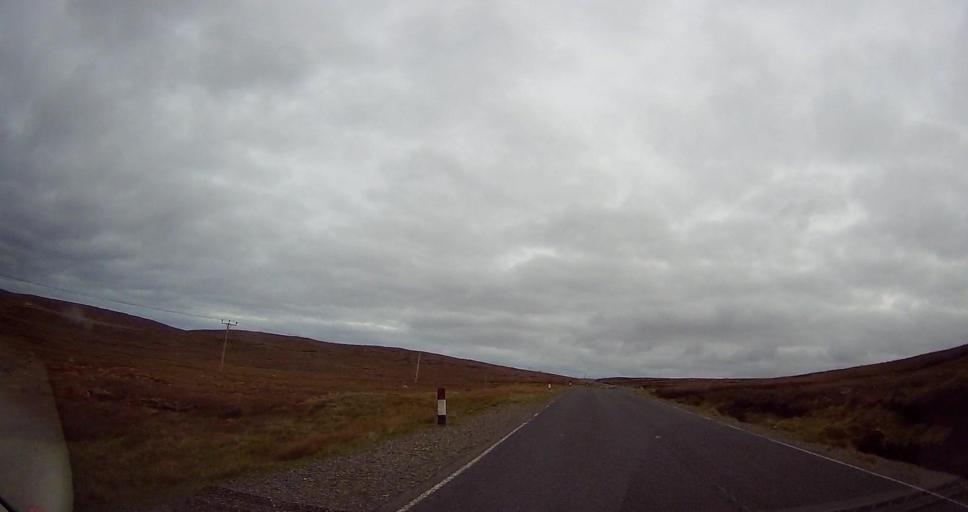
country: GB
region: Scotland
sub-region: Shetland Islands
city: Shetland
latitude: 60.6369
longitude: -1.0664
